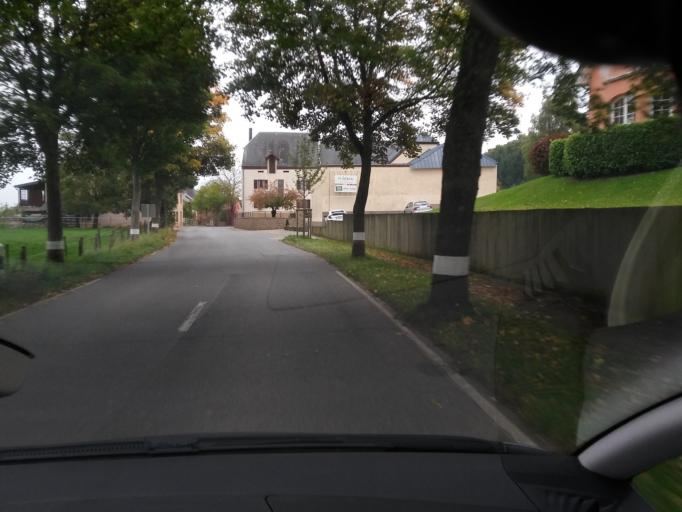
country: LU
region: Diekirch
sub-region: Canton de Redange
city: Beckerich
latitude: 49.7310
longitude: 5.8760
